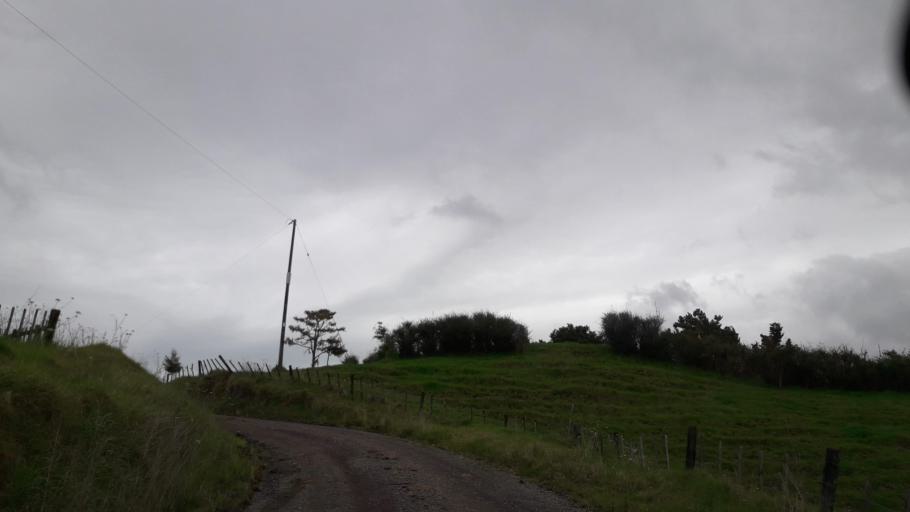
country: NZ
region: Northland
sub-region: Far North District
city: Waimate North
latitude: -35.3118
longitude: 173.5647
